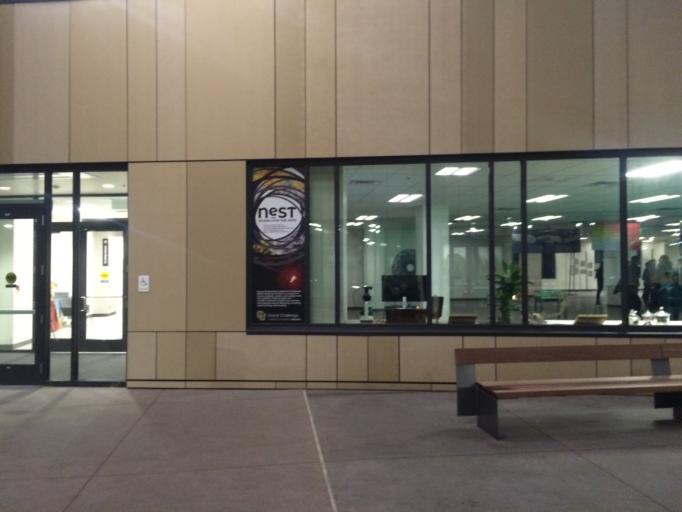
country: US
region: Colorado
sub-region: Boulder County
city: Boulder
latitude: 40.0062
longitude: -105.2703
